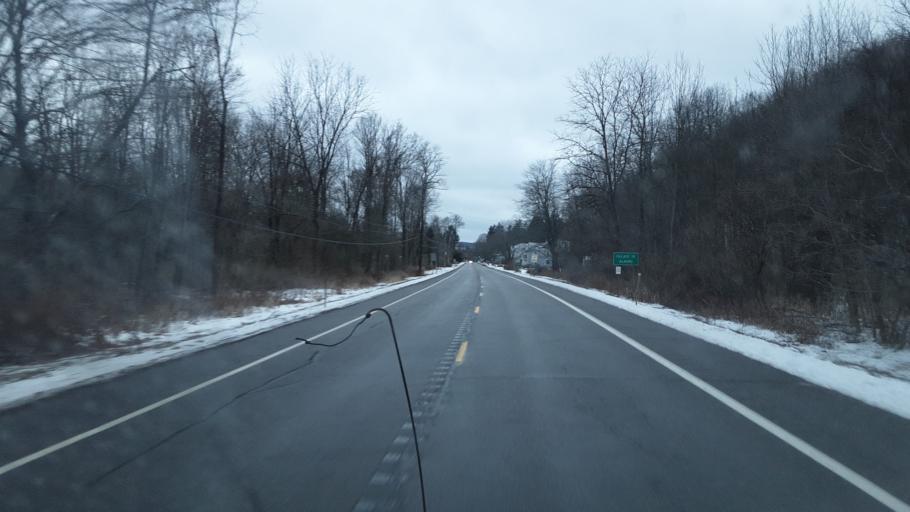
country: US
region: New York
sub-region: Steuben County
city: Hornell
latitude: 42.3306
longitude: -77.7311
